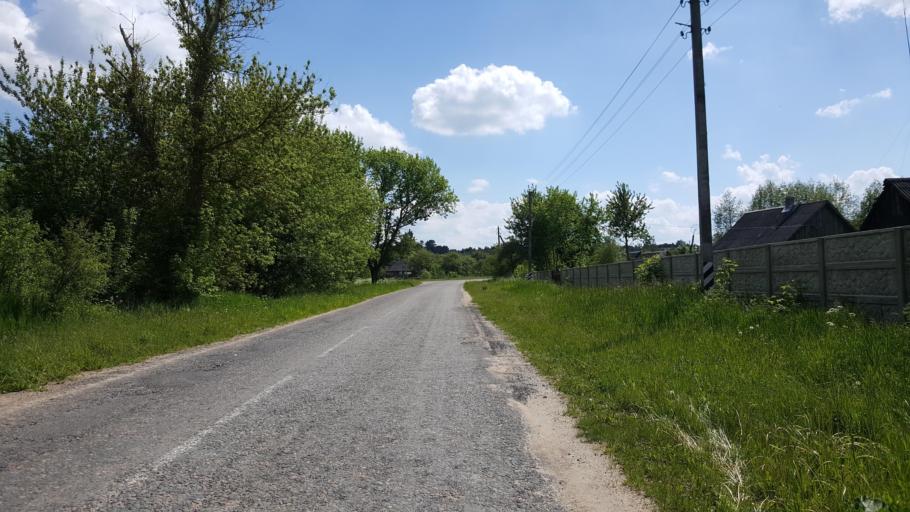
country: BY
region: Brest
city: Kamyanyets
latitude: 52.4170
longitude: 23.9321
